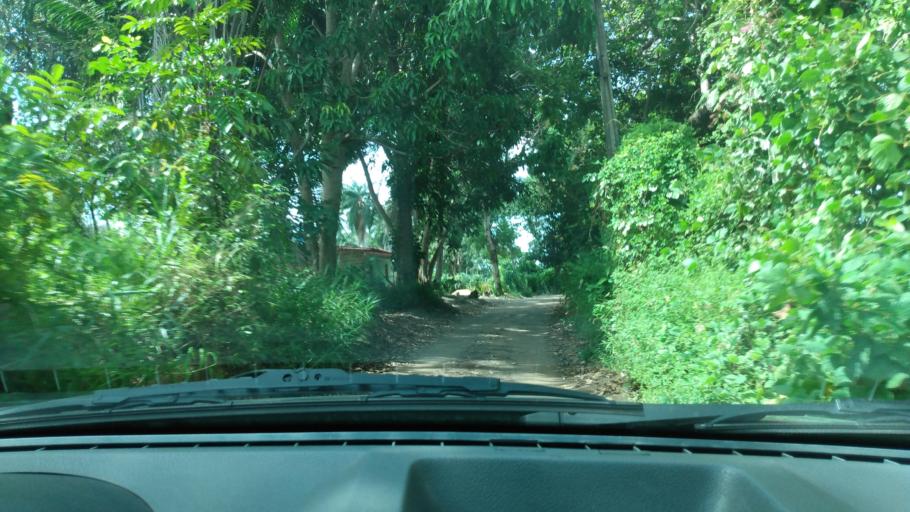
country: BR
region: Pernambuco
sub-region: Cabo De Santo Agostinho
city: Cabo
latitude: -8.3590
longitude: -34.9678
